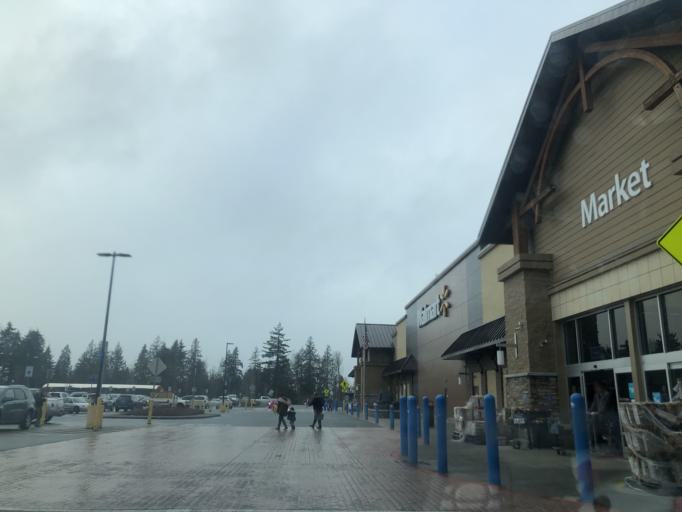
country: US
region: Washington
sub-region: Snohomish County
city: Sisco Heights
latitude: 48.0551
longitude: -122.1118
